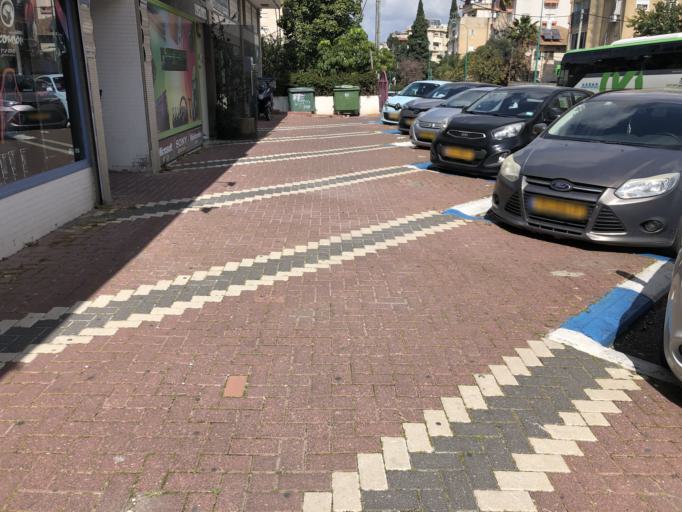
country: IL
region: Haifa
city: Hadera
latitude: 32.4377
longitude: 34.9173
